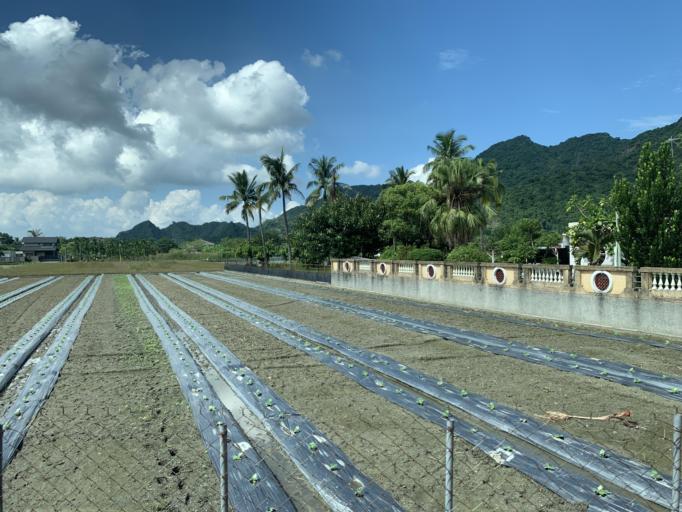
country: TW
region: Taiwan
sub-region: Pingtung
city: Pingtung
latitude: 22.8984
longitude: 120.5177
